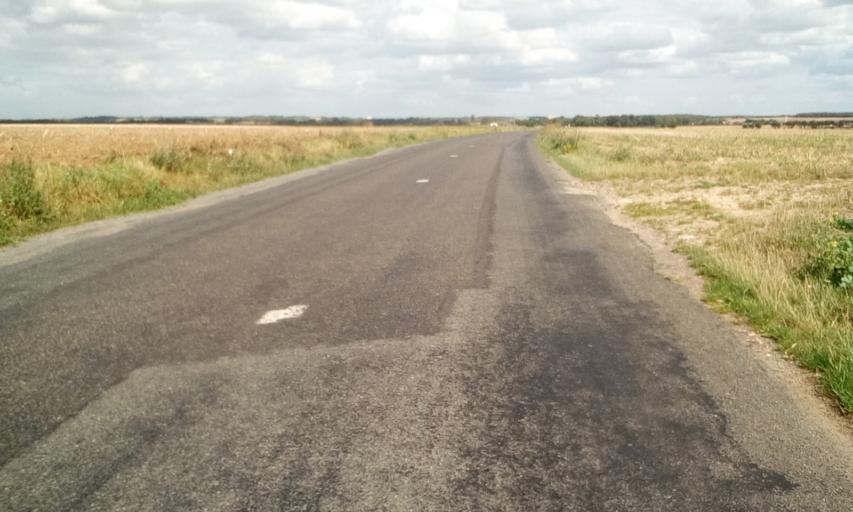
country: FR
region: Lower Normandy
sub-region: Departement du Calvados
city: Bellengreville
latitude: 49.0925
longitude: -0.2189
